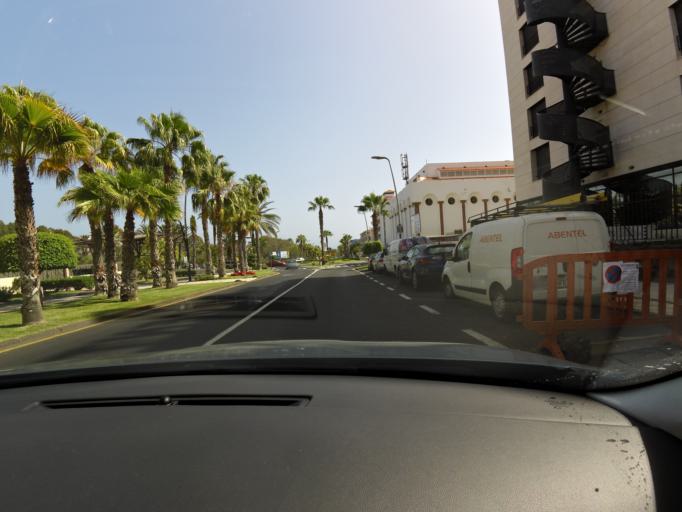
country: ES
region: Canary Islands
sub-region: Provincia de Santa Cruz de Tenerife
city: Playa de las Americas
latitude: 28.0576
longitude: -16.7280
